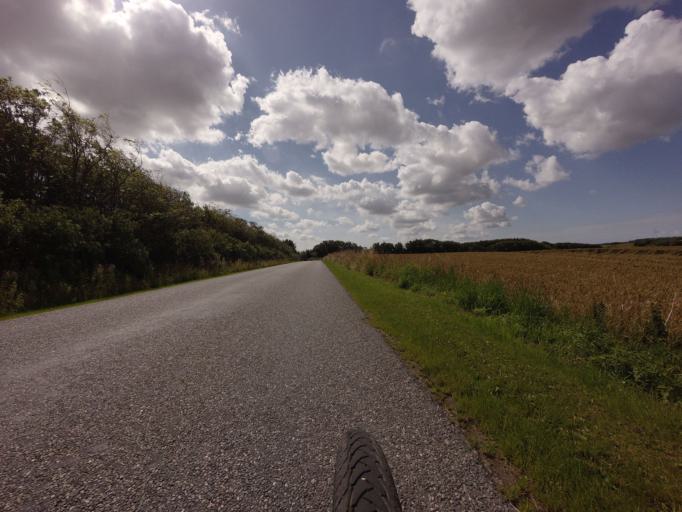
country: DK
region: North Denmark
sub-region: Hjorring Kommune
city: Hjorring
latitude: 57.4637
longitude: 9.9056
